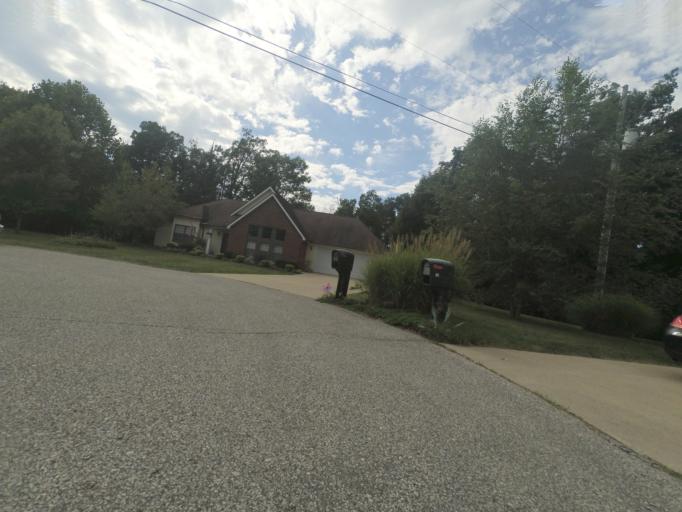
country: US
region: West Virginia
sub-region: Cabell County
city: Huntington
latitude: 38.3961
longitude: -82.4638
